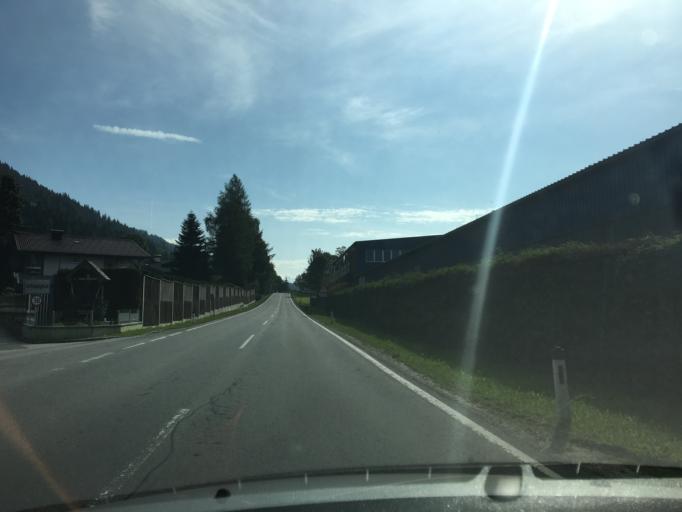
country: AT
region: Salzburg
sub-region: Politischer Bezirk Sankt Johann im Pongau
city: Wagrain
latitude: 47.3536
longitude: 13.3214
